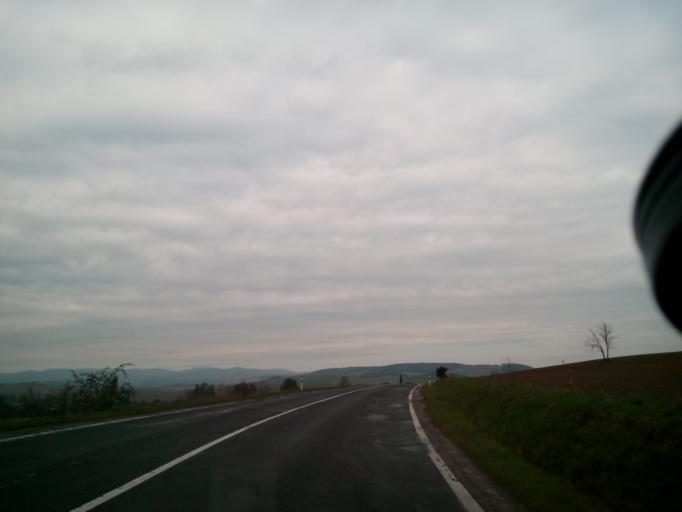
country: SK
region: Presovsky
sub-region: Okres Presov
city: Presov
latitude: 49.0815
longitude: 21.3174
